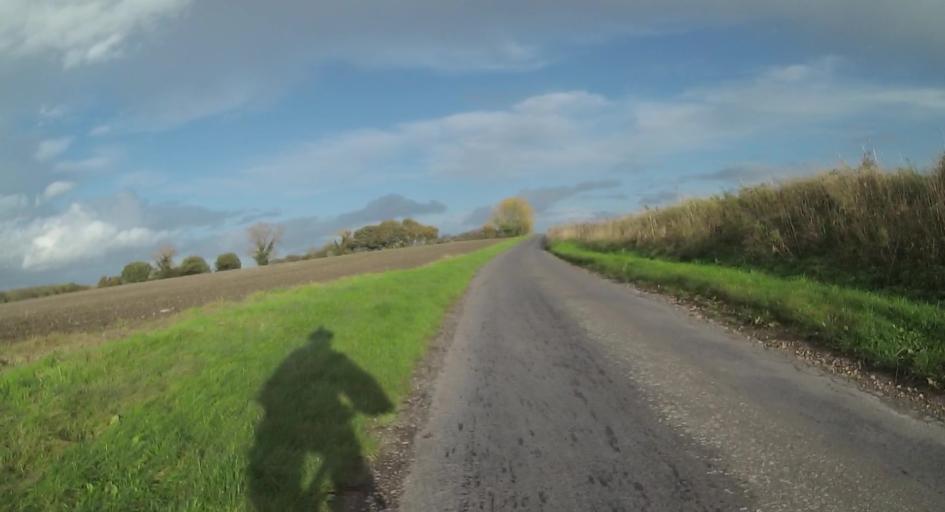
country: GB
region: England
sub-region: Hampshire
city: Kingsley
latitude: 51.1698
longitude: -0.9057
